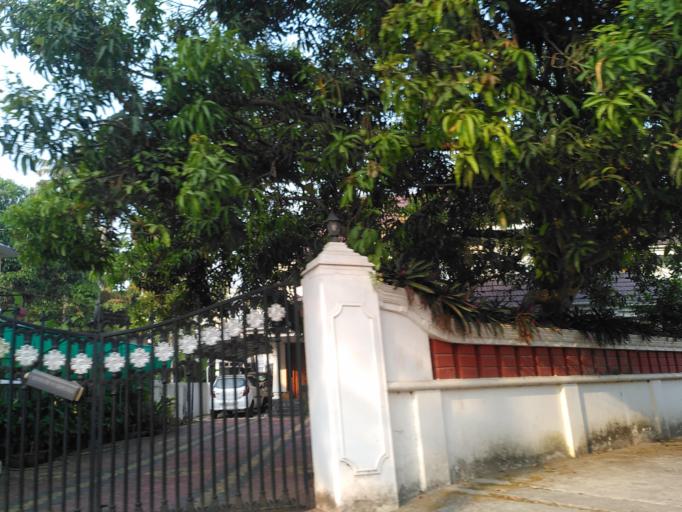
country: IN
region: Kerala
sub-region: Ernakulam
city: Cochin
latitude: 9.9371
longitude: 76.3235
